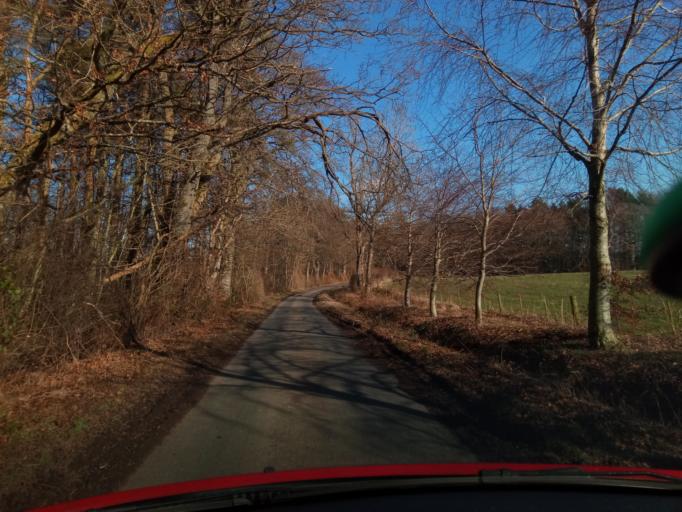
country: GB
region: Scotland
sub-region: The Scottish Borders
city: Hawick
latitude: 55.5046
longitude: -2.7648
